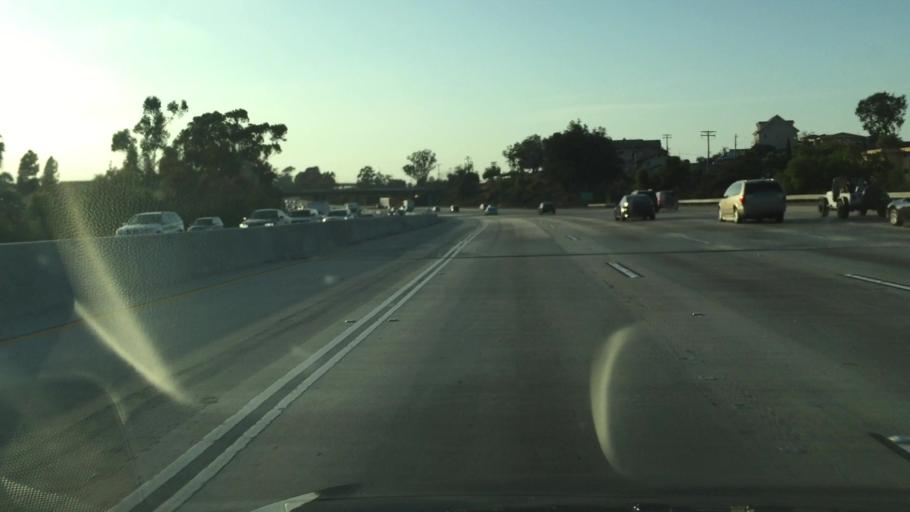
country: US
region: California
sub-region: San Diego County
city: National City
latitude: 32.6816
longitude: -117.0868
